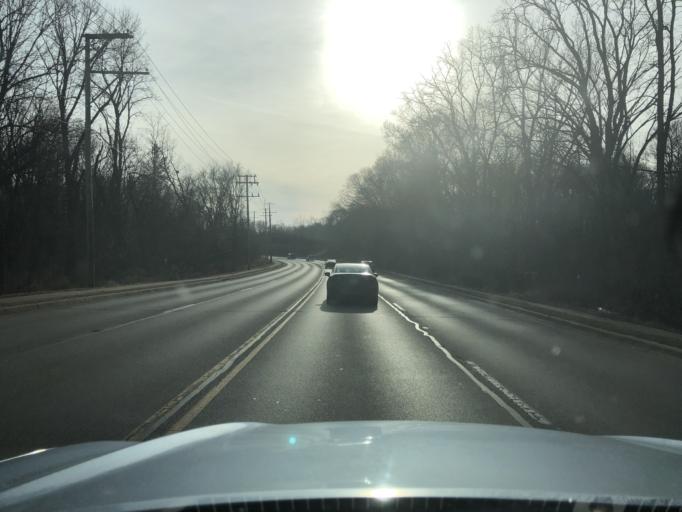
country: US
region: Illinois
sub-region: DuPage County
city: Bloomingdale
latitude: 41.9646
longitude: -88.0816
